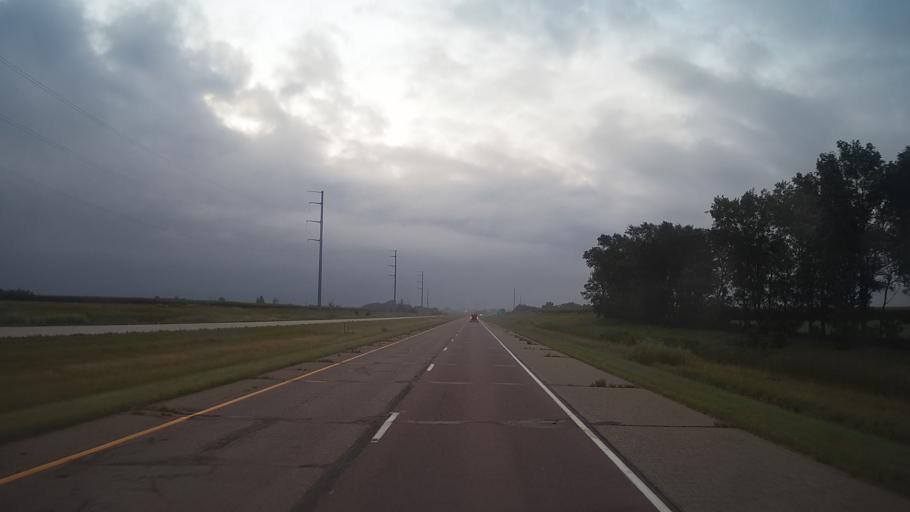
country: US
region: Minnesota
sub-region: Jackson County
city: Lakefield
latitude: 43.6373
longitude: -95.3473
